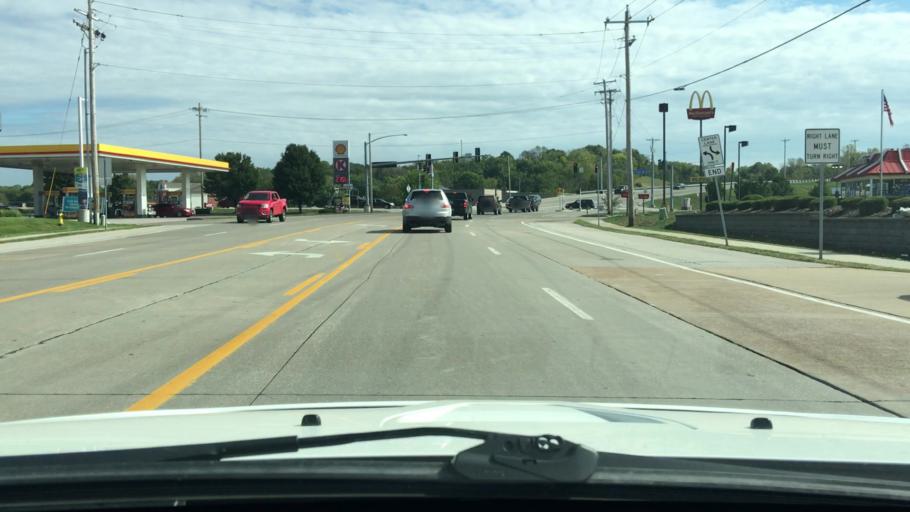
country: US
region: Missouri
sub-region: Saint Charles County
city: Saint Charles
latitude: 38.8202
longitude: -90.5143
